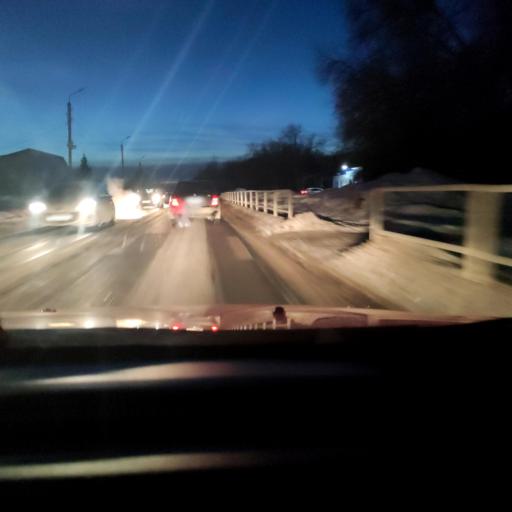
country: RU
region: Samara
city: Kinel'
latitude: 53.2694
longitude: 50.5772
